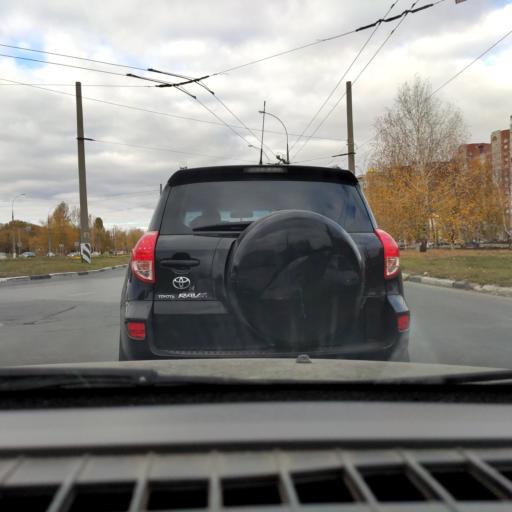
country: RU
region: Samara
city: Tol'yatti
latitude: 53.4987
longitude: 49.2911
